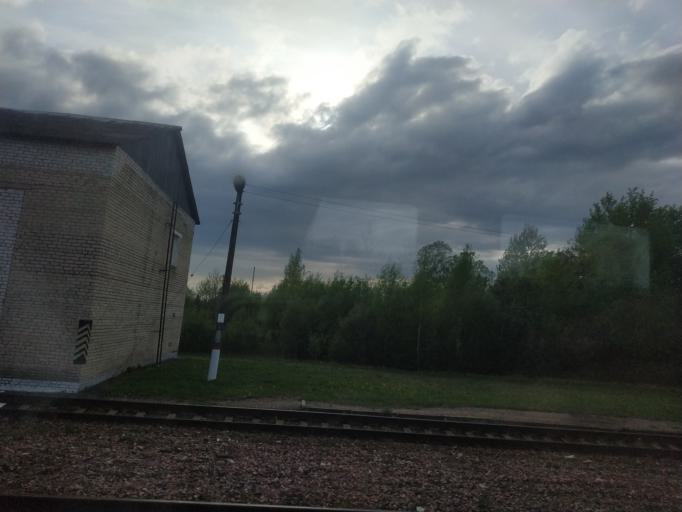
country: RU
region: Smolensk
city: Ugra
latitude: 54.7772
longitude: 34.3424
